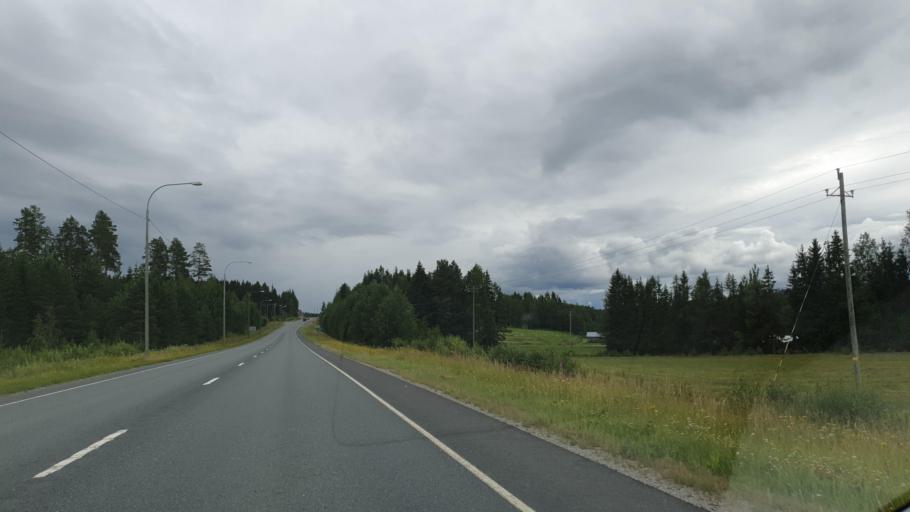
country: FI
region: Northern Savo
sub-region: Ylae-Savo
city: Lapinlahti
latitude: 63.3121
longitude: 27.4474
